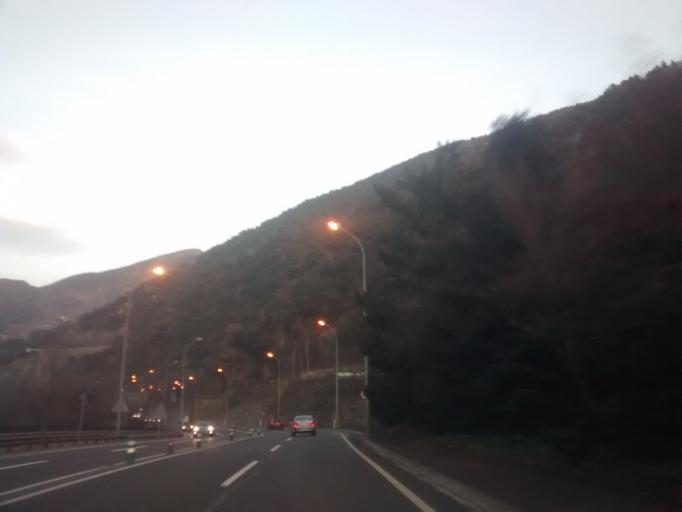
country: AD
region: Sant Julia de Loria
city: Sant Julia de Loria
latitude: 42.4418
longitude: 1.4785
